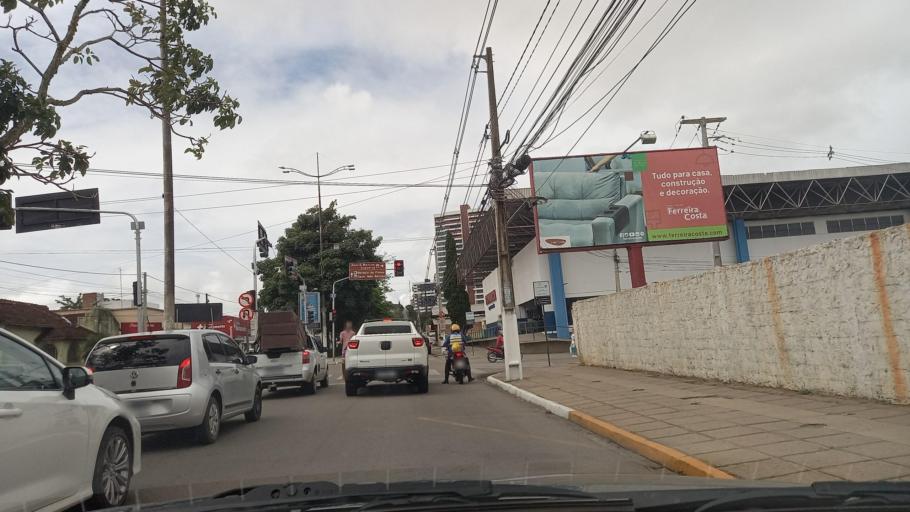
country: BR
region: Pernambuco
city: Garanhuns
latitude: -8.8833
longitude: -36.4796
